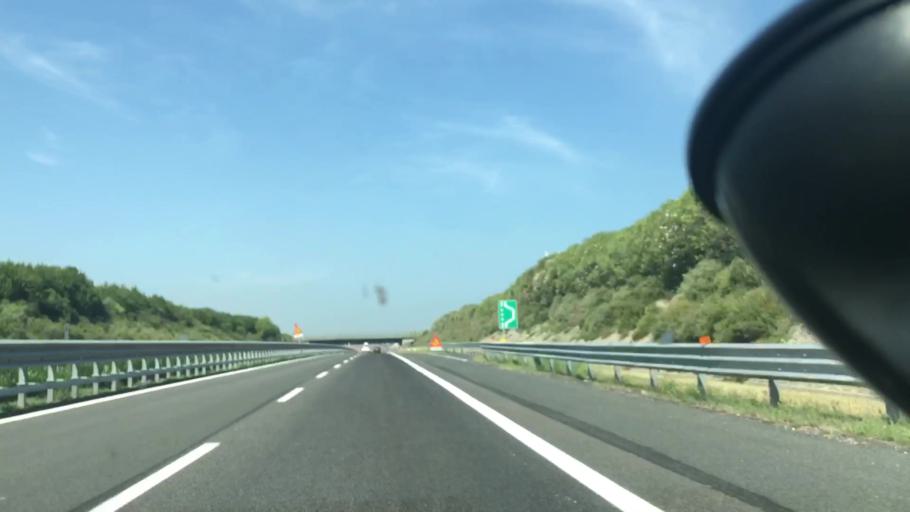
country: IT
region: Molise
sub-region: Provincia di Campobasso
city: Campomarino
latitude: 41.9465
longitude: 15.0277
